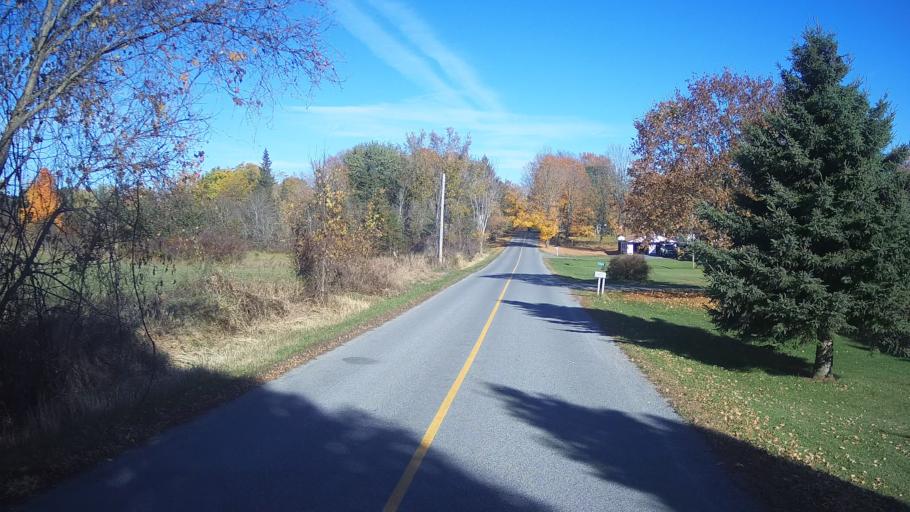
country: CA
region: Ontario
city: Kingston
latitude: 44.4482
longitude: -76.5154
